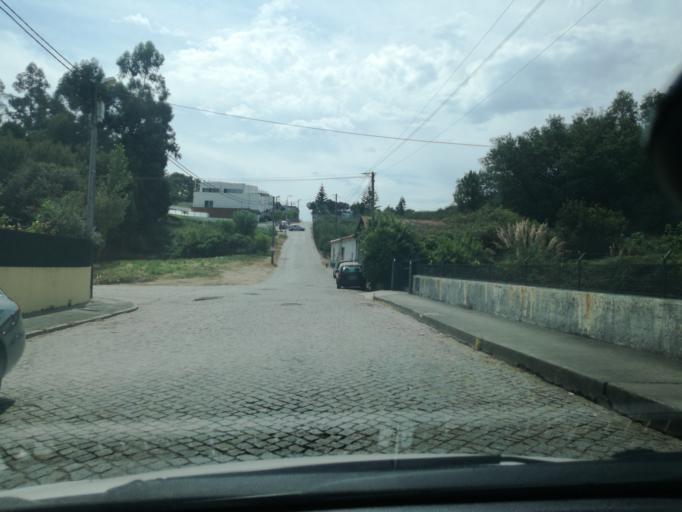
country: PT
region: Porto
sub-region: Vila Nova de Gaia
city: Grijo
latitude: 41.0207
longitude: -8.5861
